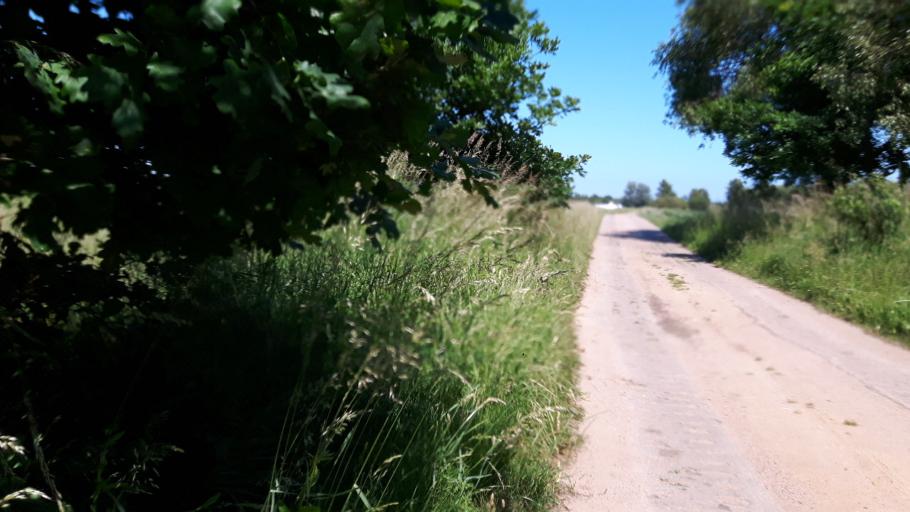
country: PL
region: Pomeranian Voivodeship
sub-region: Powiat slupski
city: Glowczyce
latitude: 54.6405
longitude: 17.3579
